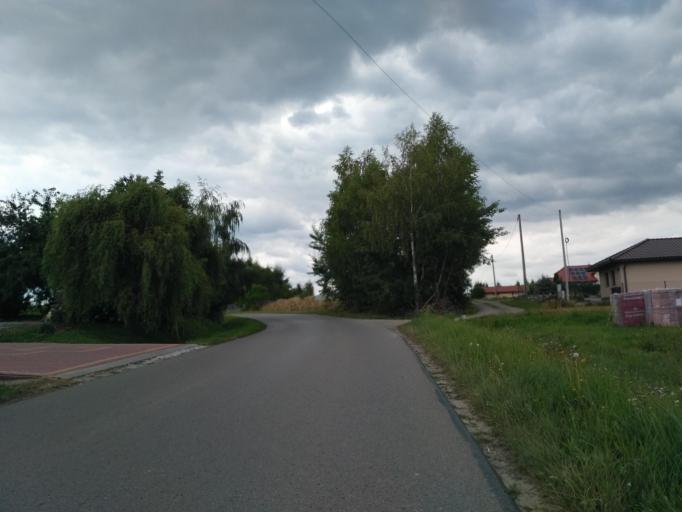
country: PL
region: Subcarpathian Voivodeship
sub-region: Powiat rzeszowski
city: Tyczyn
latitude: 49.9333
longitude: 22.0408
